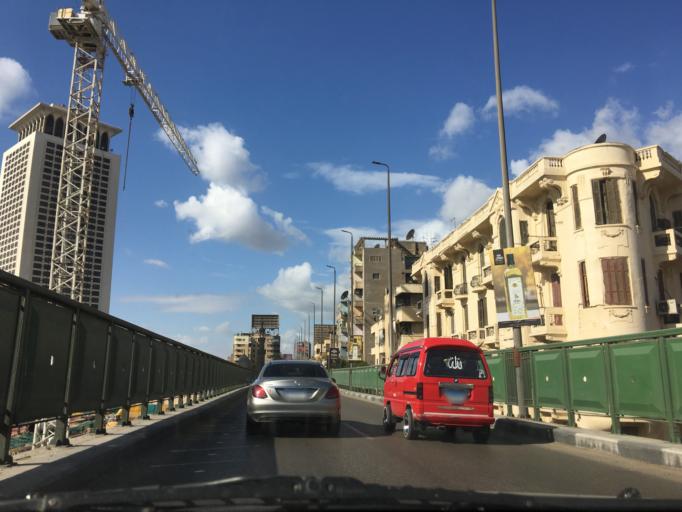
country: EG
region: Muhafazat al Qahirah
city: Cairo
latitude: 30.0555
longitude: 31.2330
